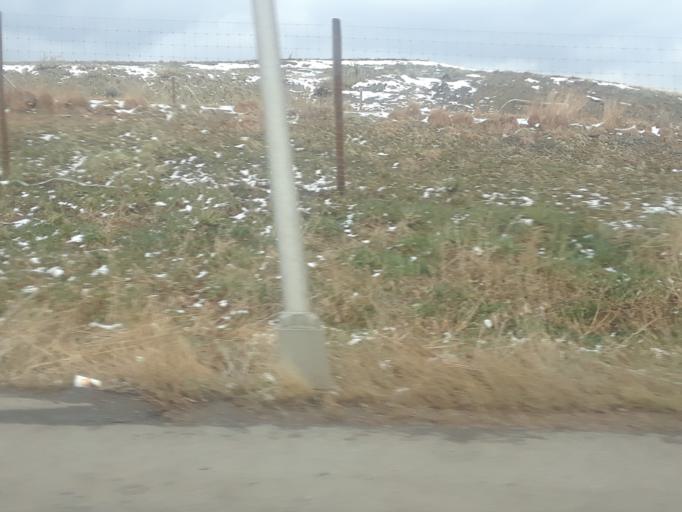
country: US
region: Colorado
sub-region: Jefferson County
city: Golden
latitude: 39.7407
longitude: -105.2194
